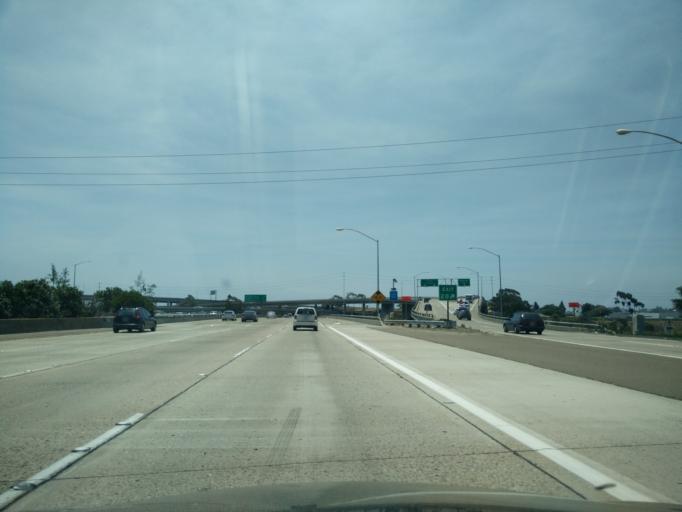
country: US
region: California
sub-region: San Diego County
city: San Diego
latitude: 32.7631
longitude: -117.2051
